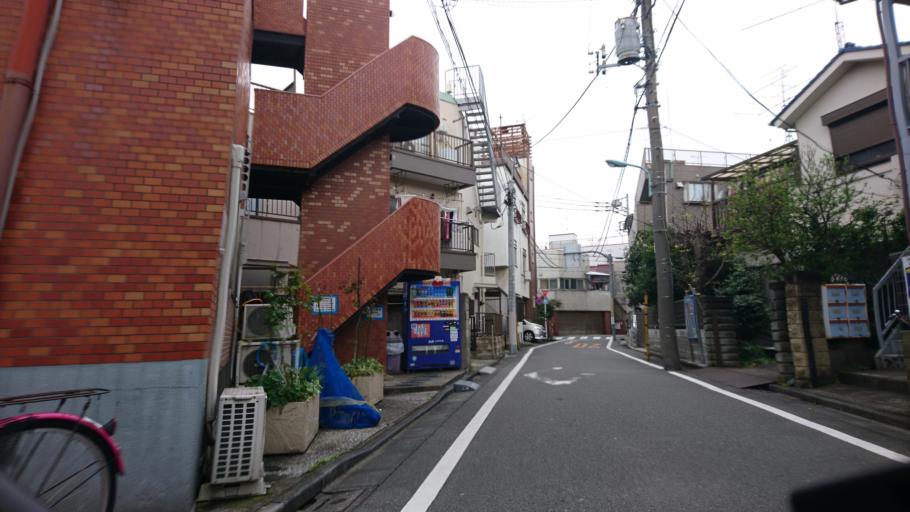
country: JP
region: Kanagawa
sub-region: Kawasaki-shi
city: Kawasaki
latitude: 35.5499
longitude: 139.7241
